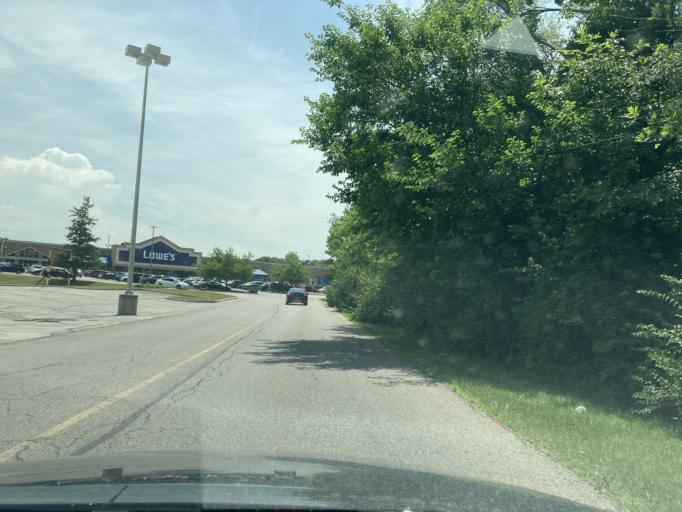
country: US
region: Indiana
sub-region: Marion County
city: Broad Ripple
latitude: 39.8647
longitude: -86.1211
